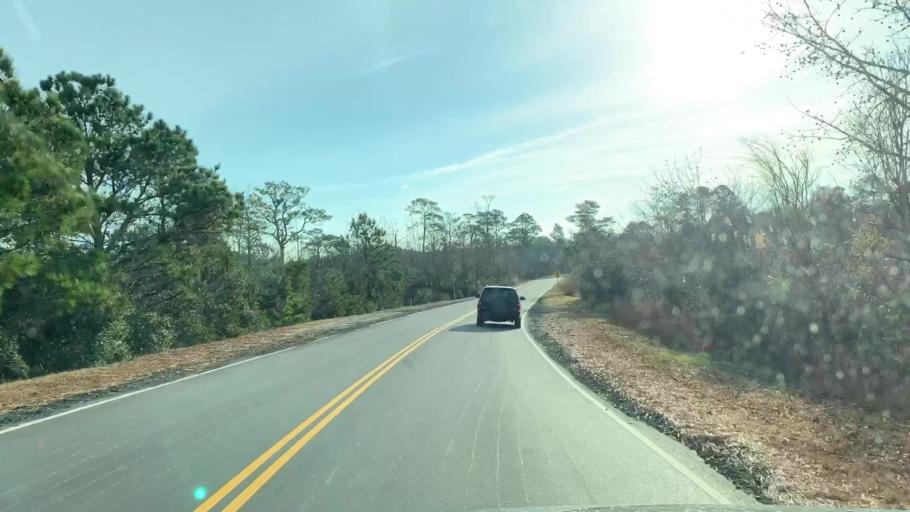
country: US
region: Virginia
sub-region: City of Virginia Beach
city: Virginia Beach
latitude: 36.6948
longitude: -76.0398
